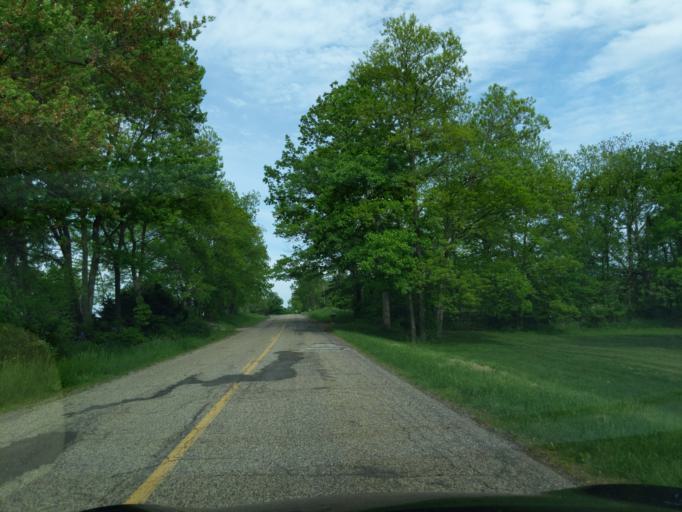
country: US
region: Michigan
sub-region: Ingham County
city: Leslie
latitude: 42.4167
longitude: -84.3446
